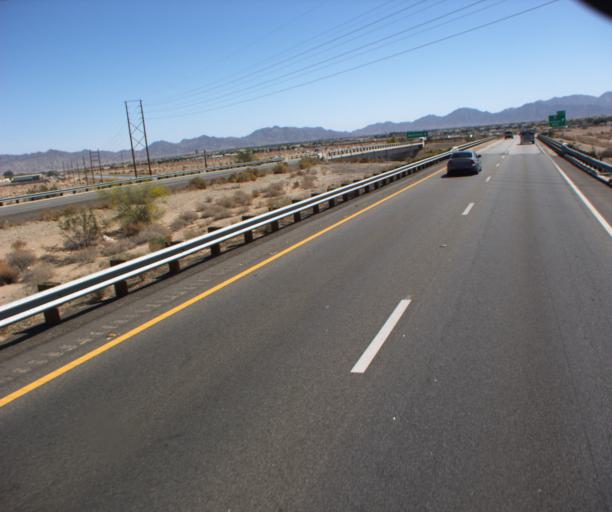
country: US
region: Arizona
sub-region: Yuma County
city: Fortuna Foothills
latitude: 32.6743
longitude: -114.4932
